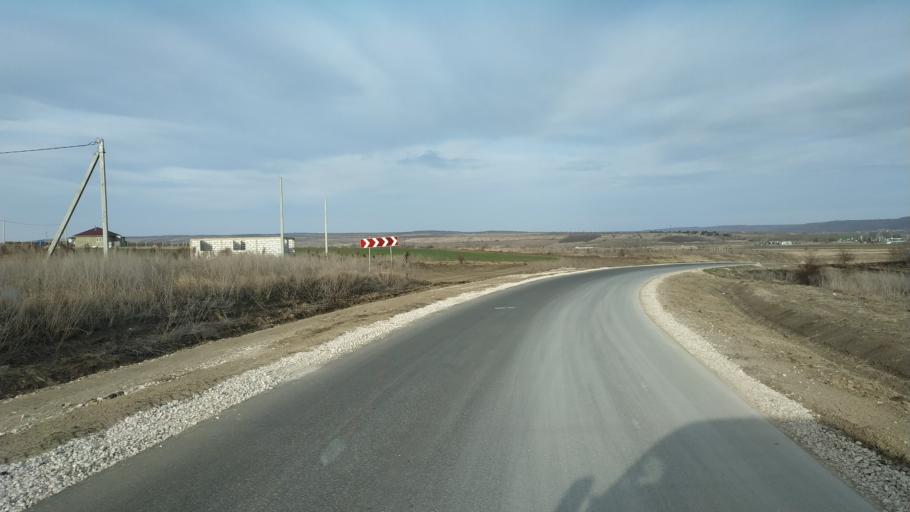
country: RO
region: Vaslui
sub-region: Comuna Dranceni
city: Dranceni
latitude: 46.8465
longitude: 28.1914
